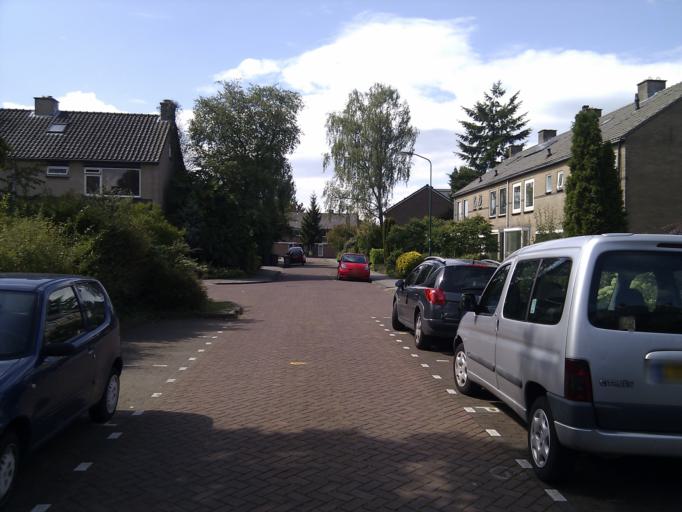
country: NL
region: Utrecht
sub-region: Gemeente De Bilt
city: De Bilt
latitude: 52.1251
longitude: 5.1985
